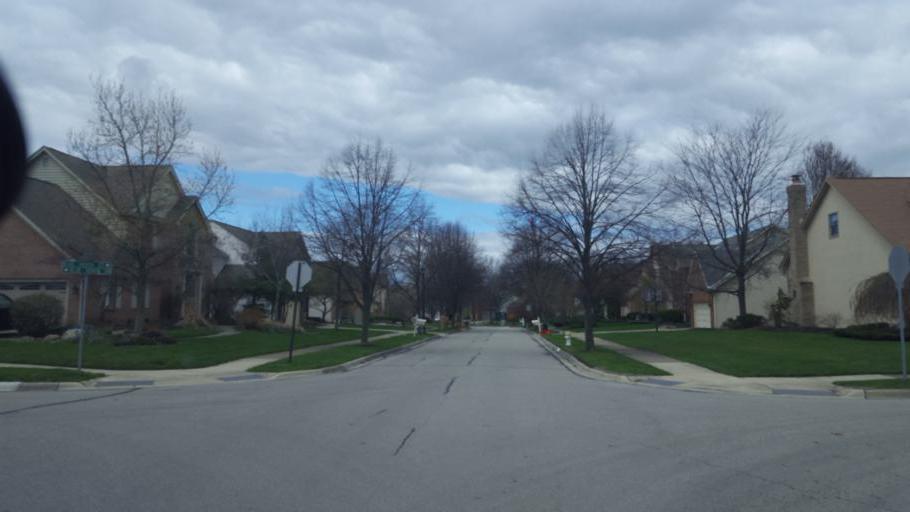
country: US
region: Ohio
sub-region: Franklin County
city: Westerville
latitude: 40.1377
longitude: -82.8863
